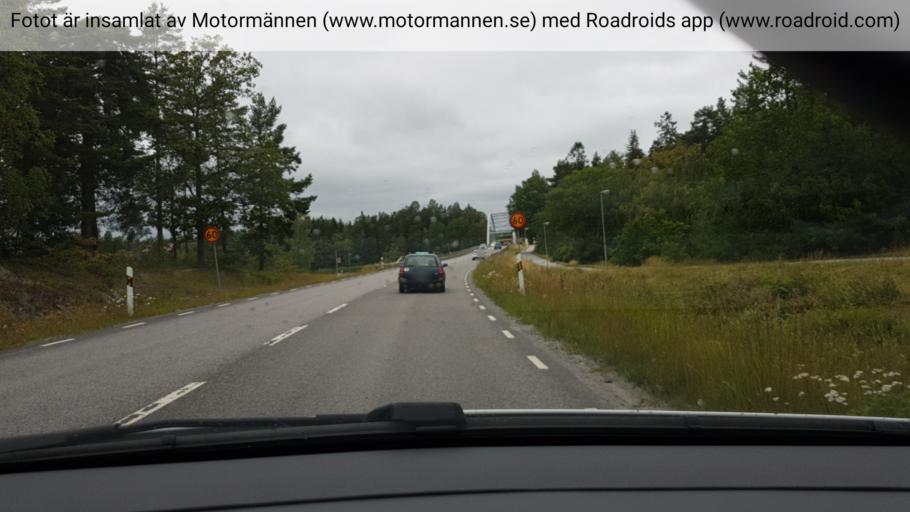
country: SE
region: Stockholm
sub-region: Vaxholms Kommun
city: Resaro
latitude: 59.4072
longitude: 18.3171
